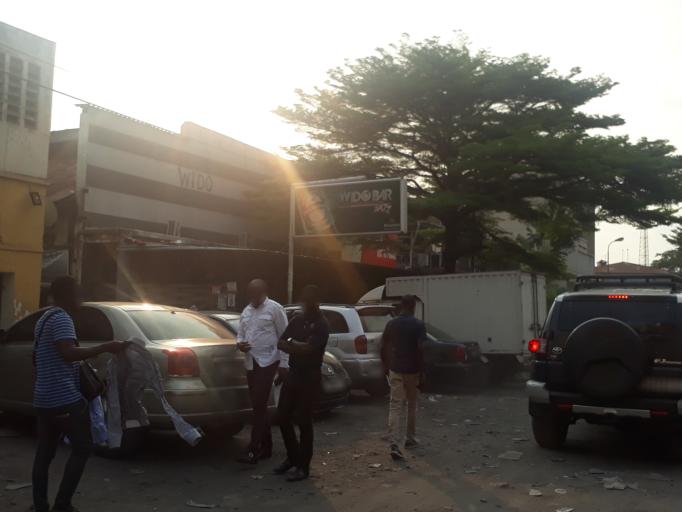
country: CD
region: Kinshasa
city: Kinshasa
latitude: -4.3012
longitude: 15.3118
